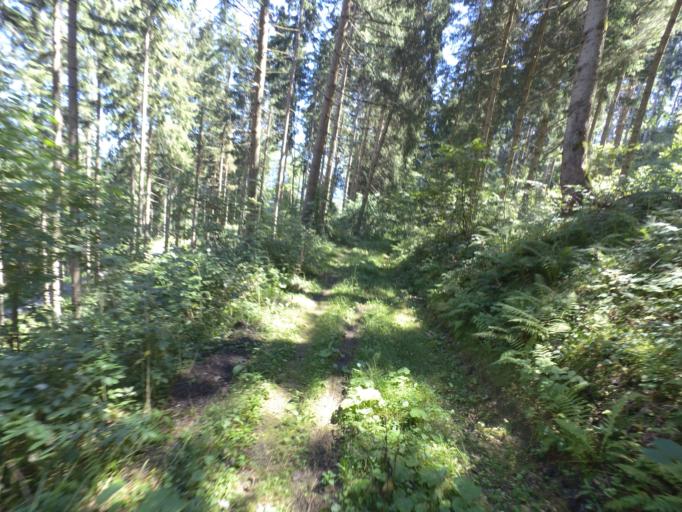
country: AT
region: Salzburg
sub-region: Politischer Bezirk Sankt Johann im Pongau
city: Sankt Veit im Pongau
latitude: 47.3264
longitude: 13.1257
